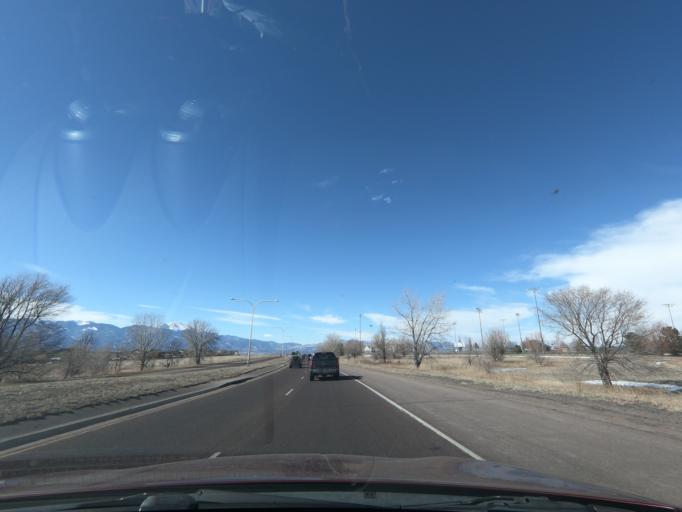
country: US
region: Colorado
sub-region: El Paso County
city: Security-Widefield
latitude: 38.7854
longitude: -104.7232
